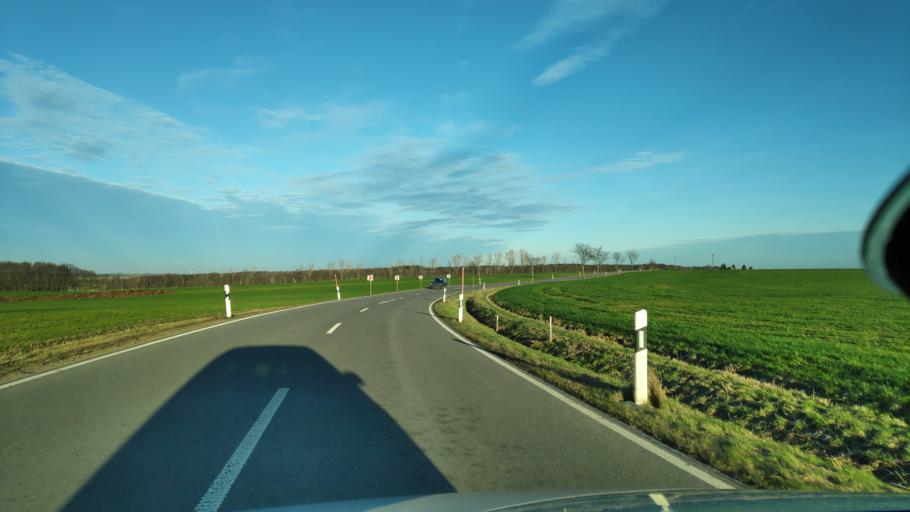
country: DE
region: Thuringia
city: Seelingstadt
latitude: 50.8018
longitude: 12.2669
